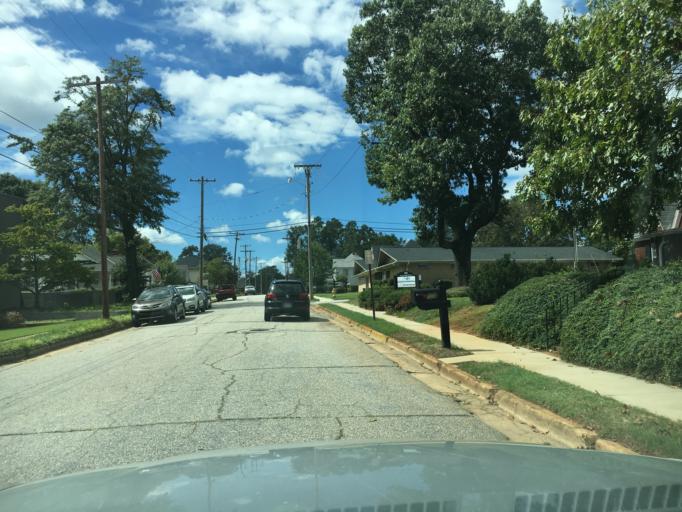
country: US
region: South Carolina
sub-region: Greenville County
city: Greer
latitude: 34.9405
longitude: -82.2268
